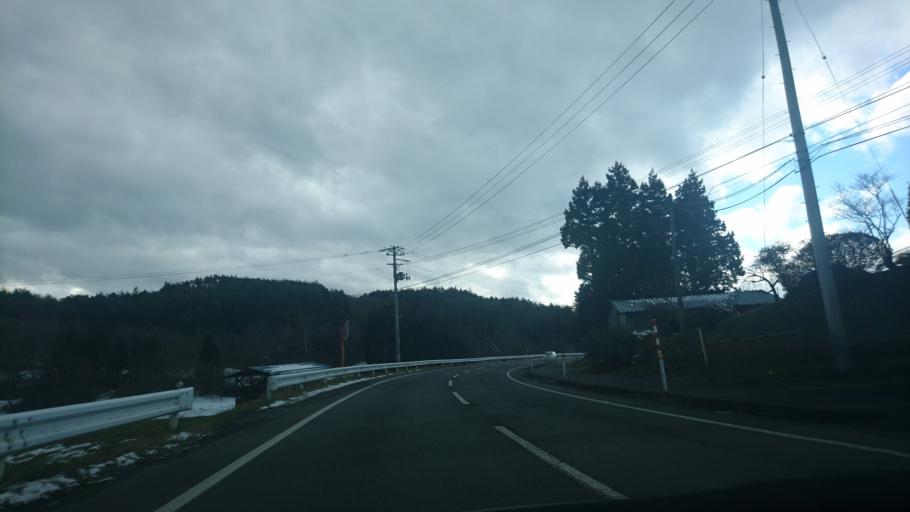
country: JP
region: Iwate
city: Mizusawa
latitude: 39.1467
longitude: 141.2090
